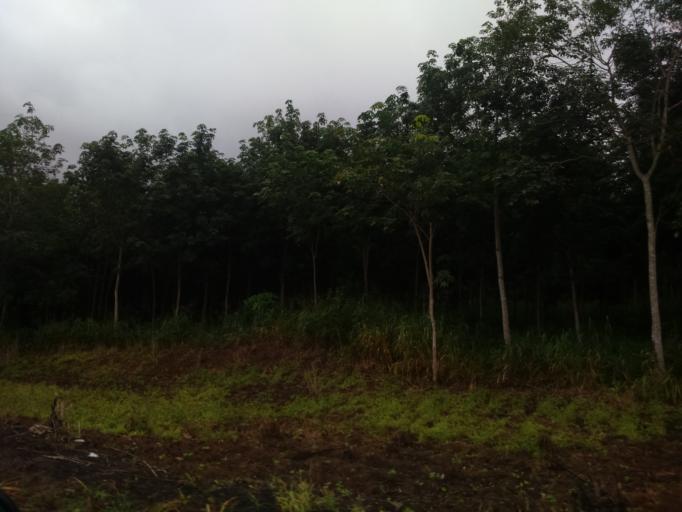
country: CI
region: Sud-Comoe
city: Adiake
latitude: 5.2999
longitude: -3.3462
